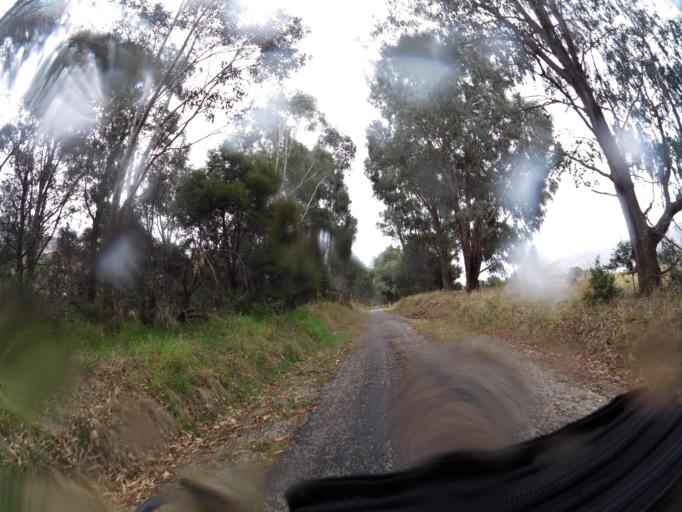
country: AU
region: New South Wales
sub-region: Albury Municipality
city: East Albury
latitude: -36.2163
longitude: 147.1941
